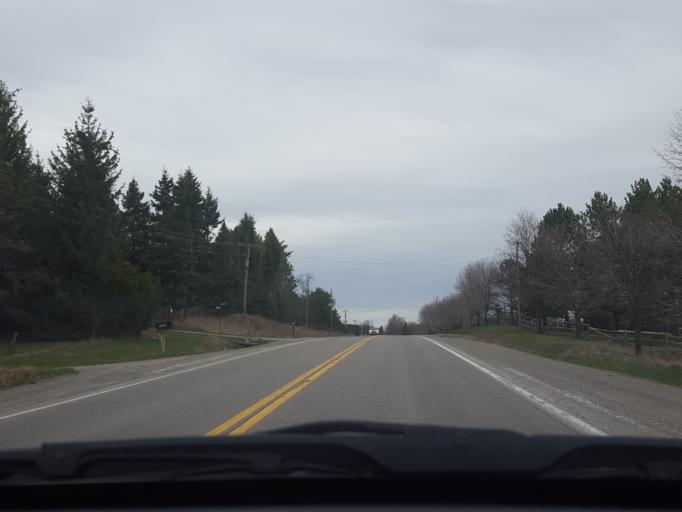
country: CA
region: Ontario
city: Uxbridge
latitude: 44.2043
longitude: -79.1234
